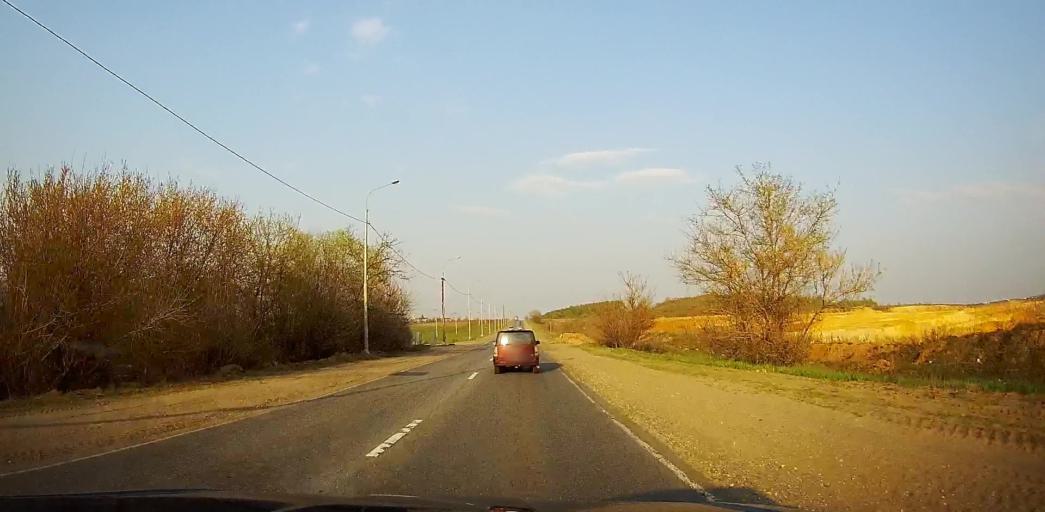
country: RU
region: Moskovskaya
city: Ostrovtsy
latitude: 55.5433
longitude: 38.0554
